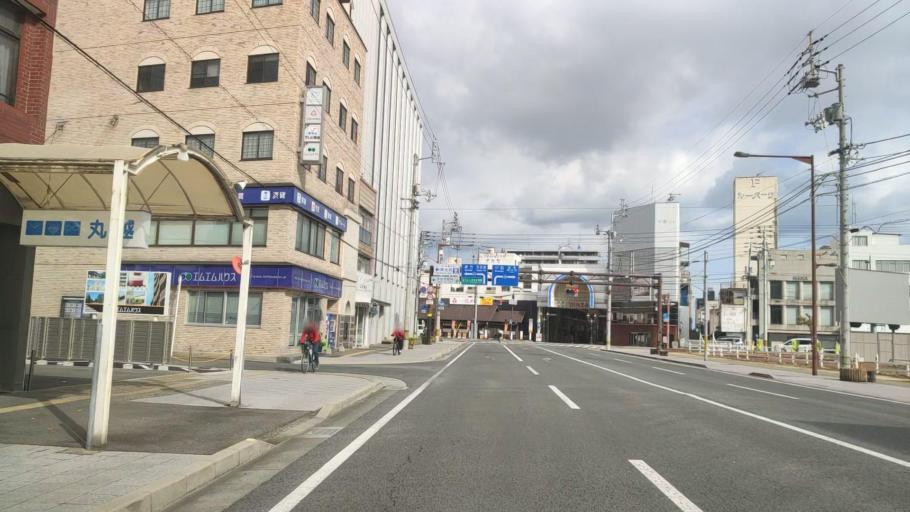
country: JP
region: Ehime
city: Saijo
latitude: 34.0649
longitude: 132.9985
